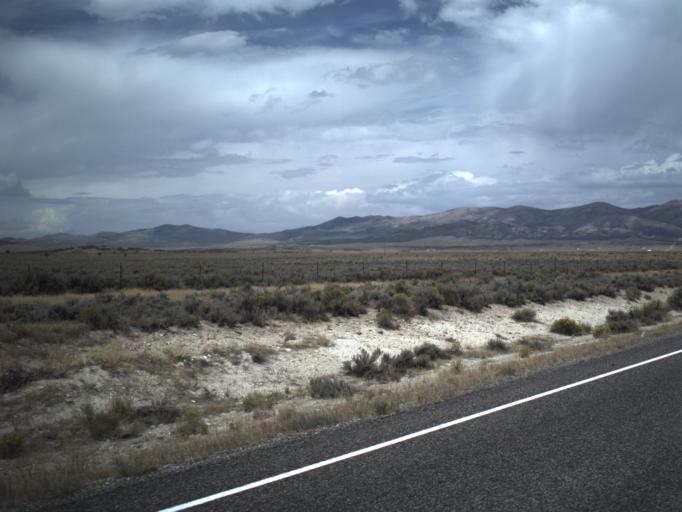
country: US
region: Idaho
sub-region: Cassia County
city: Burley
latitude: 41.7393
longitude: -113.5199
